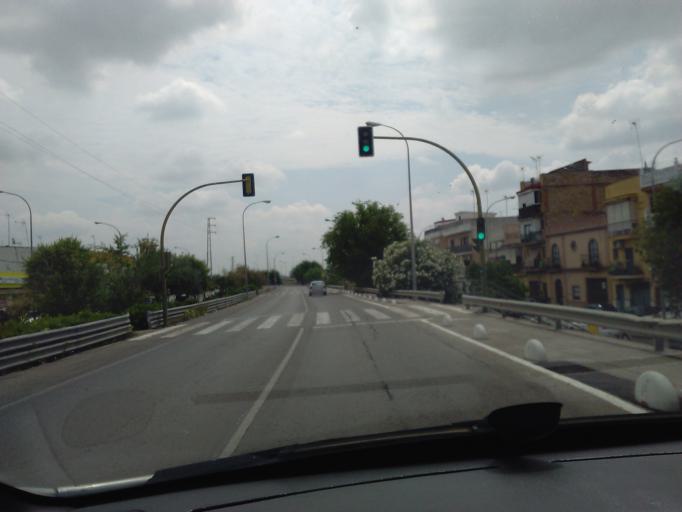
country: ES
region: Andalusia
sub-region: Provincia de Sevilla
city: Sevilla
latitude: 37.3716
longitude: -5.9428
